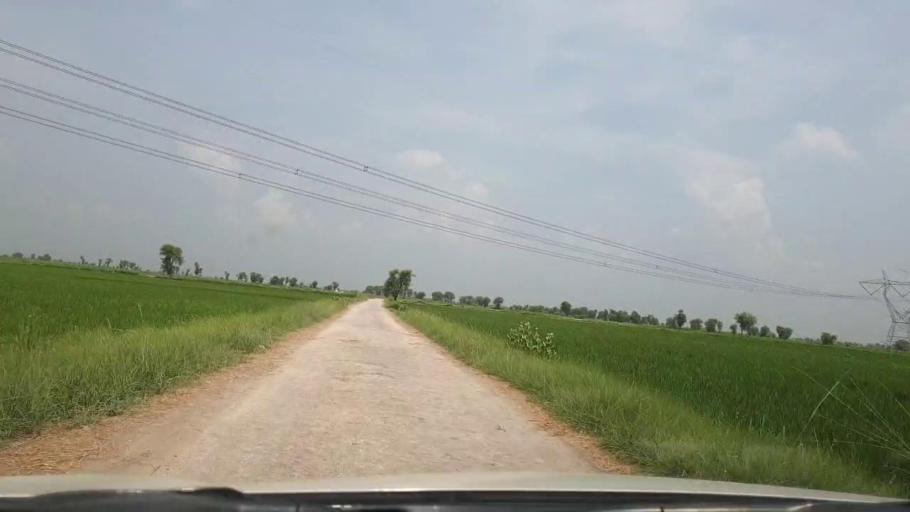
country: PK
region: Sindh
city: Dokri
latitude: 27.3909
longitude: 68.0548
